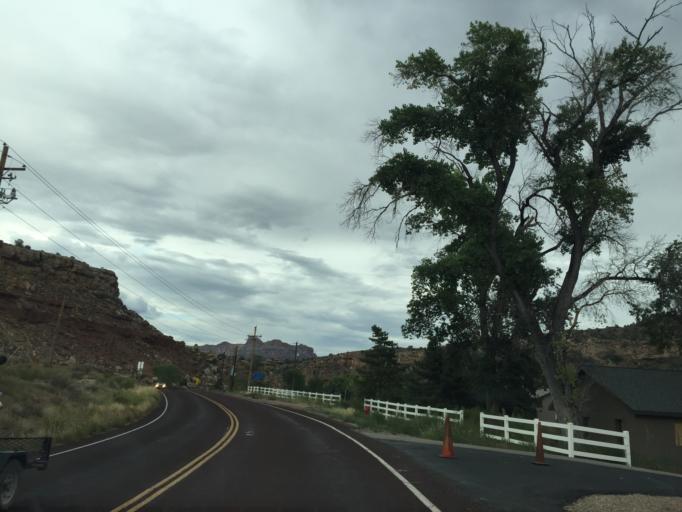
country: US
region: Utah
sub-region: Washington County
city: Hildale
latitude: 37.1610
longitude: -113.0342
